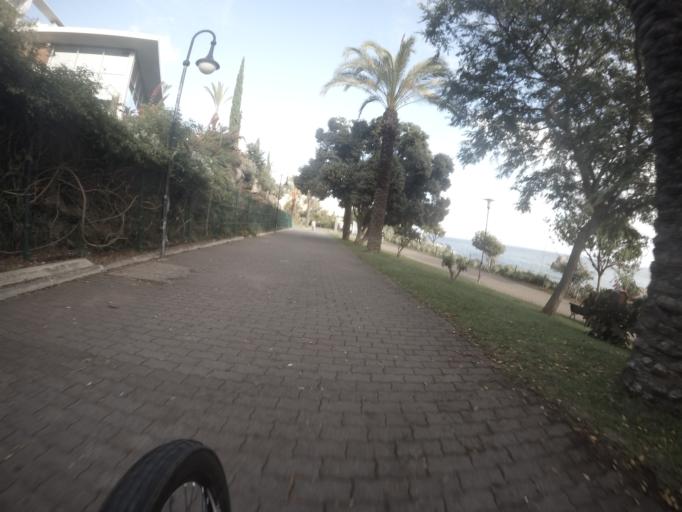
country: PT
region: Madeira
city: Camara de Lobos
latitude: 32.6365
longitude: -16.9377
